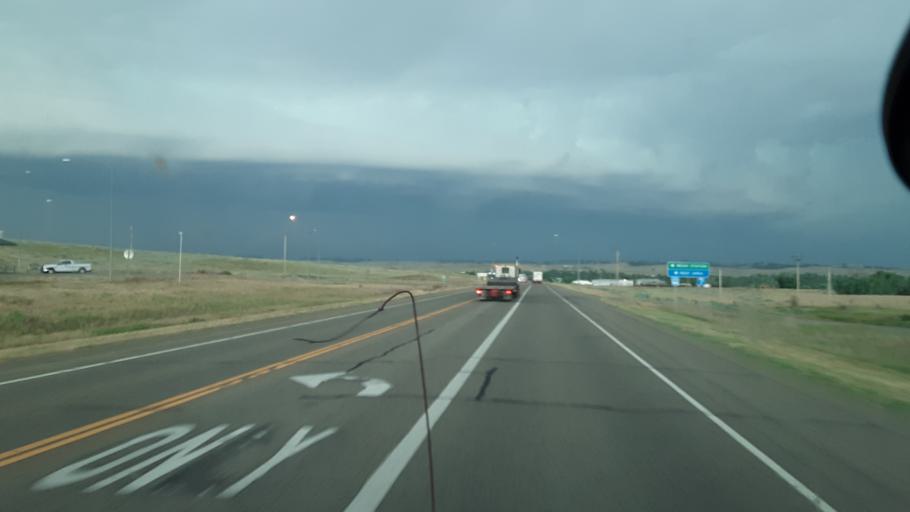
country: US
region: Montana
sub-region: Powder River County
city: Broadus
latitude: 45.4222
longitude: -105.3955
